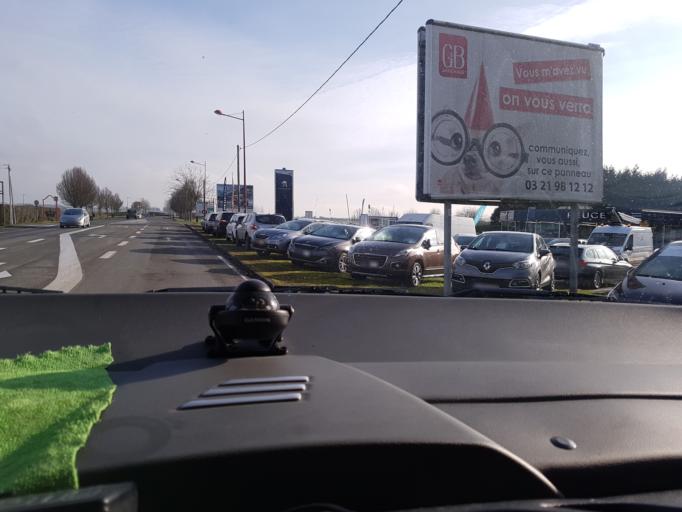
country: FR
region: Picardie
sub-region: Departement de l'Aisne
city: Hirson
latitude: 49.9069
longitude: 4.0932
